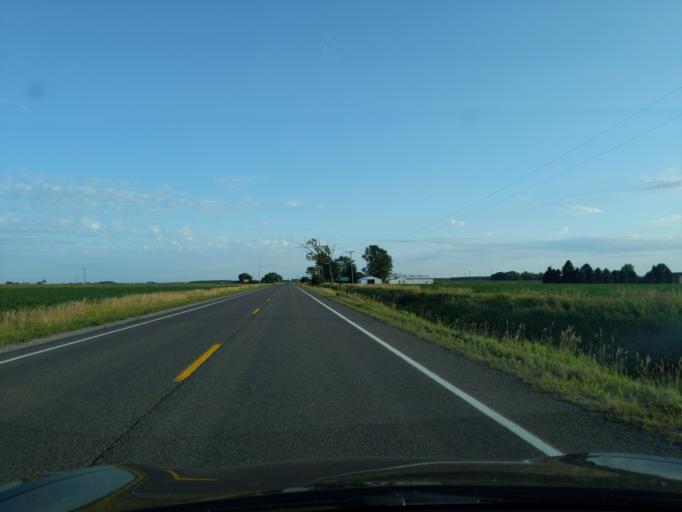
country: US
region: Michigan
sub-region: Gratiot County
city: Breckenridge
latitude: 43.4978
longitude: -84.3701
